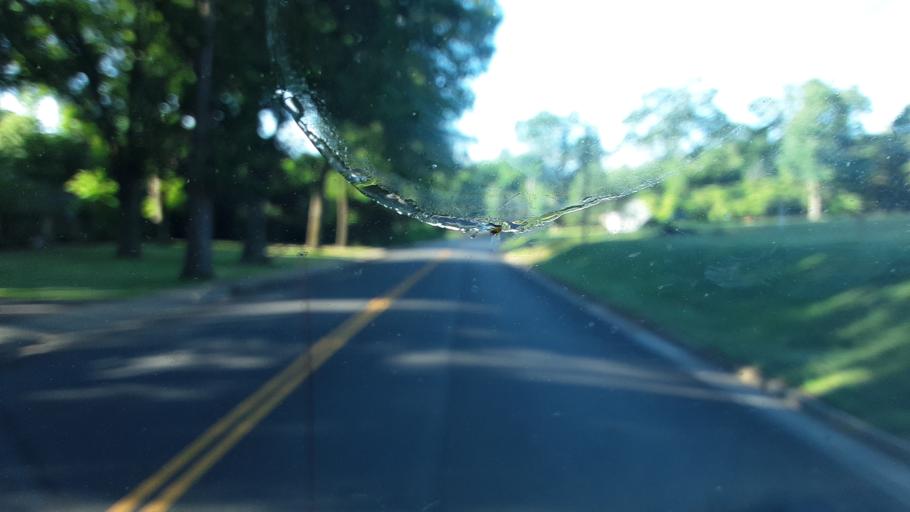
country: US
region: Virginia
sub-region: Pittsylvania County
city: Chatham
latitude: 36.8172
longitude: -79.3960
